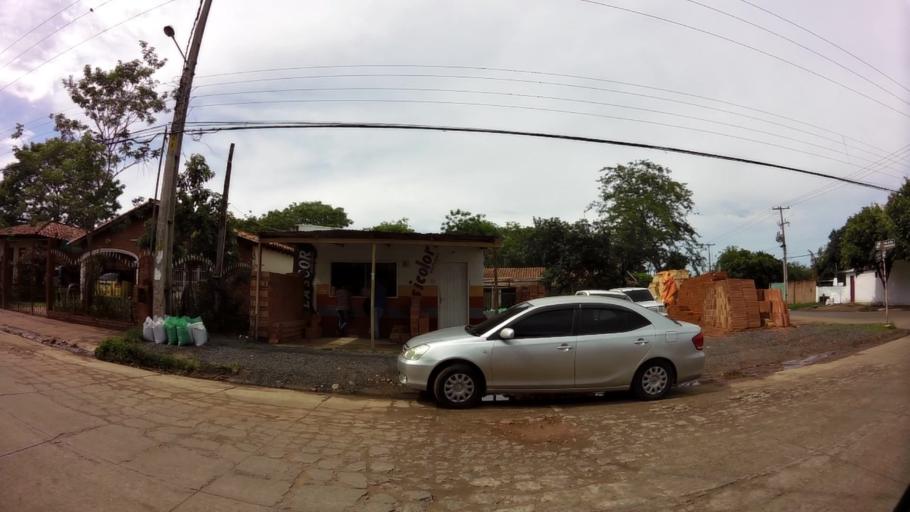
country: PY
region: Central
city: Limpio
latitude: -25.1745
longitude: -57.4737
